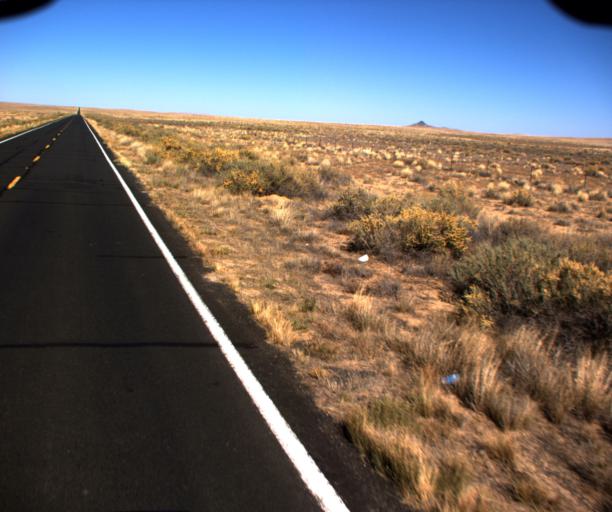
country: US
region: Arizona
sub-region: Navajo County
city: Dilkon
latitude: 35.5777
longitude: -110.4627
